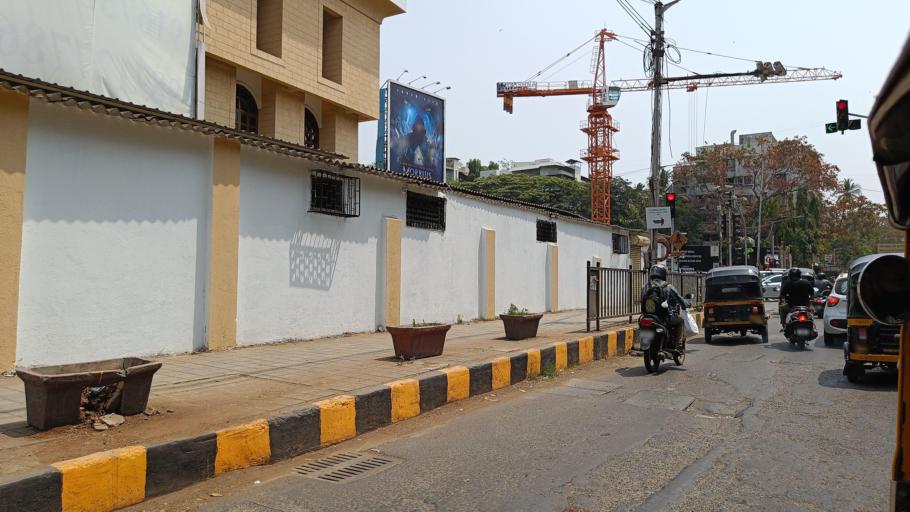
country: IN
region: Maharashtra
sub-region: Mumbai Suburban
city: Mumbai
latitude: 19.0846
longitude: 72.8340
